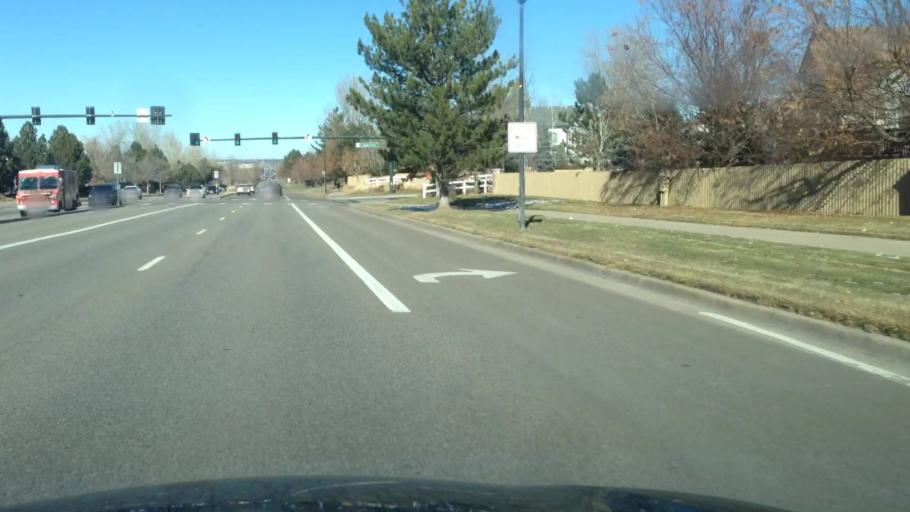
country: US
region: Colorado
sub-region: Douglas County
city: Stonegate
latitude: 39.5174
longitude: -104.7933
